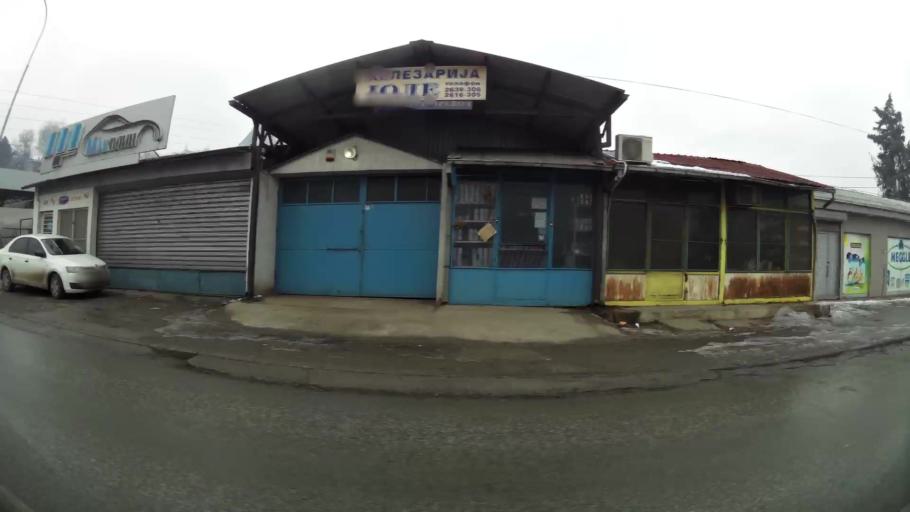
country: MK
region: Cair
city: Cair
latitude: 42.0175
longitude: 21.4532
